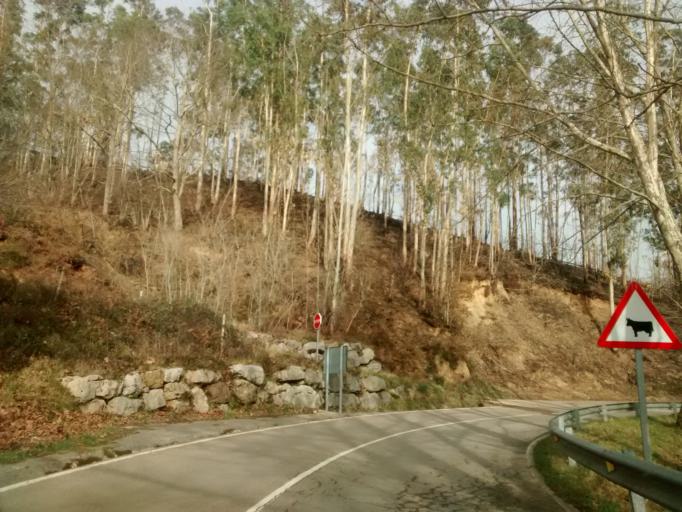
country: ES
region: Cantabria
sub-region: Provincia de Cantabria
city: Ruente
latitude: 43.2601
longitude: -4.3420
